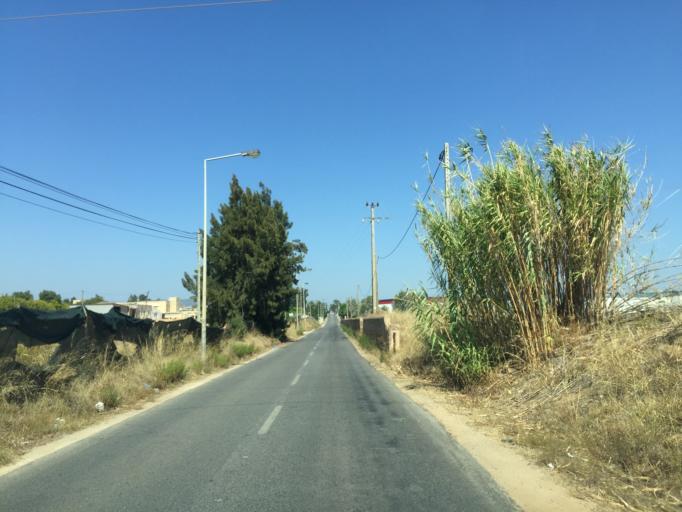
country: PT
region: Faro
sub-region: Faro
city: Faro
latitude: 37.0339
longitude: -7.9016
